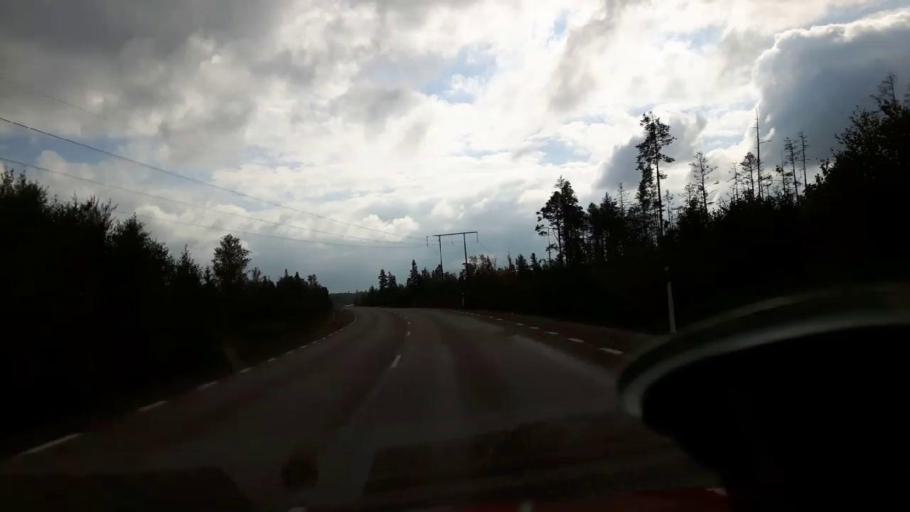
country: SE
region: Gaevleborg
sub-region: Soderhamns Kommun
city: Ljusne
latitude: 61.0903
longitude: 16.9546
